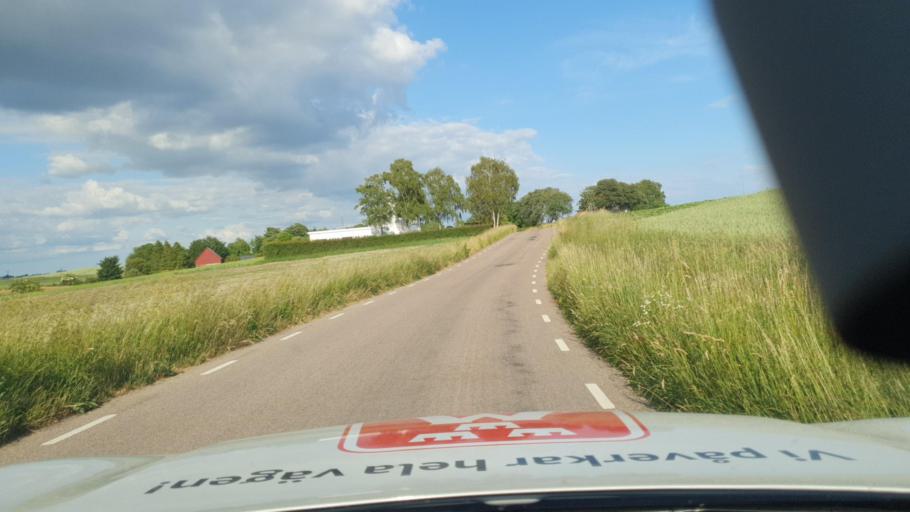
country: SE
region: Skane
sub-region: Ystads Kommun
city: Ystad
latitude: 55.4465
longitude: 13.7023
